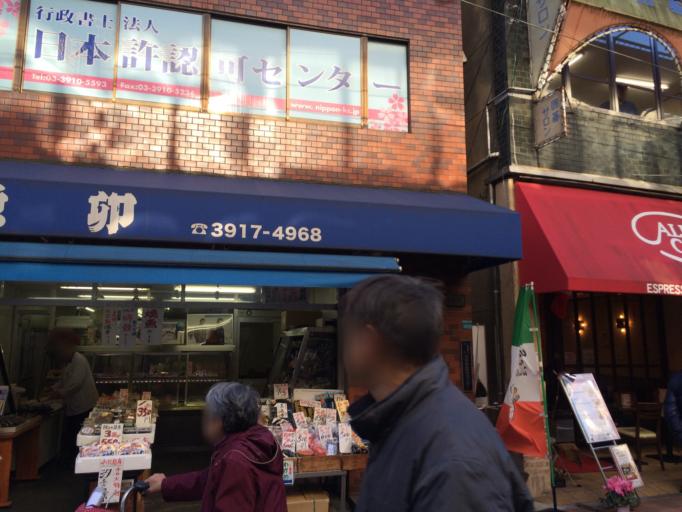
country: JP
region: Tokyo
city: Tokyo
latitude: 35.7359
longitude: 139.7348
